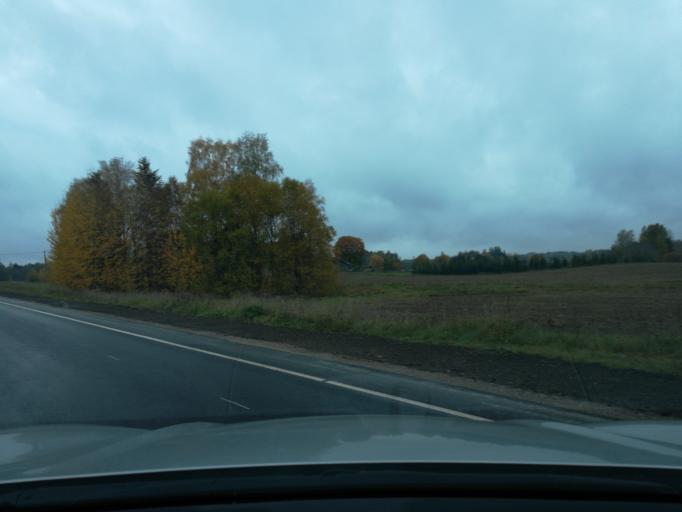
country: EE
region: Ida-Virumaa
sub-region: Johvi vald
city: Johvi
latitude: 59.1466
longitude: 27.3579
